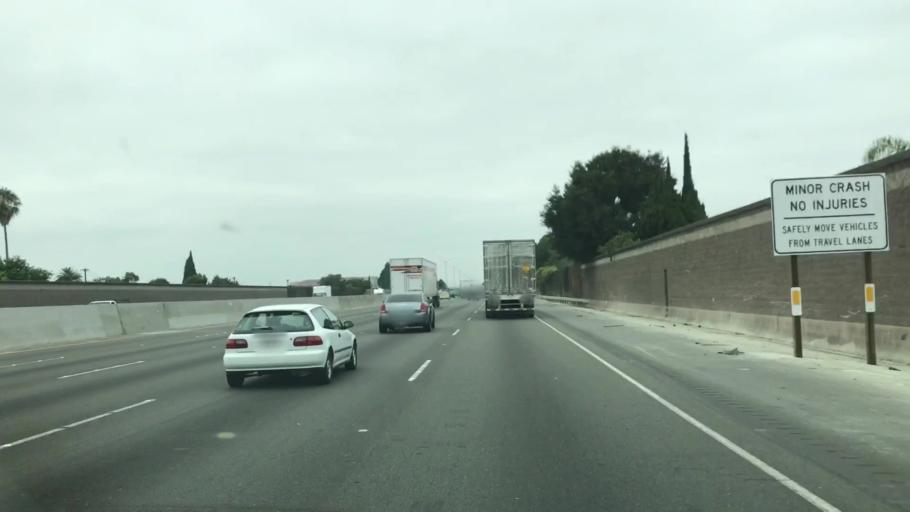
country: US
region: California
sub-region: Alameda County
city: San Leandro
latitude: 37.7010
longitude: -122.1526
